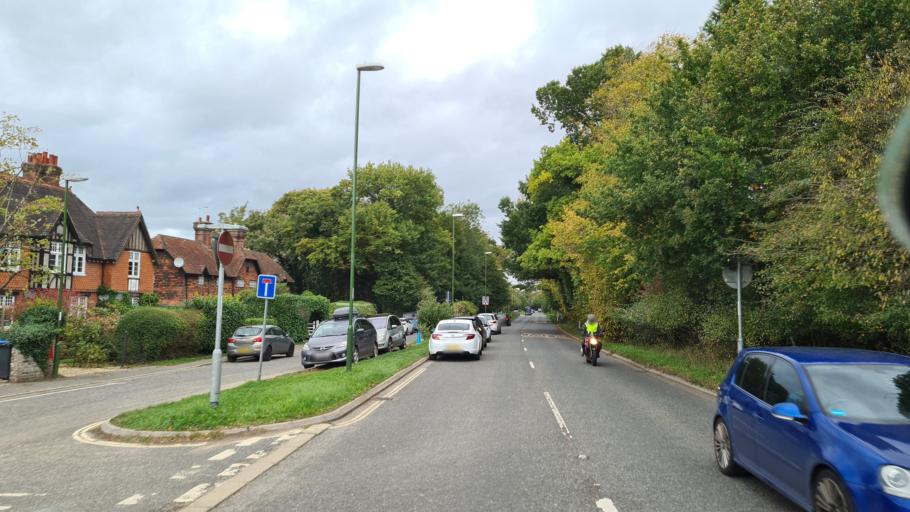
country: GB
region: England
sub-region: West Sussex
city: Broadfield
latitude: 51.0607
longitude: -0.1995
